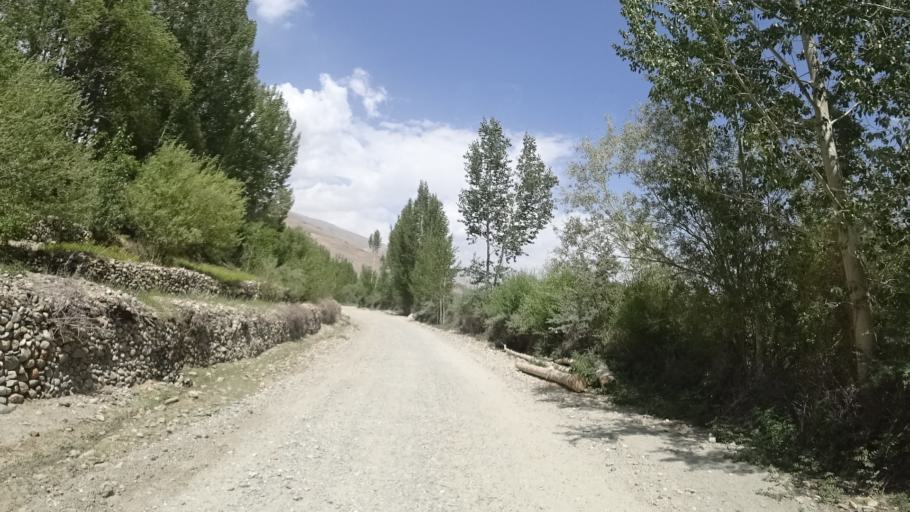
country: AF
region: Badakhshan
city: Khandud
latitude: 36.9420
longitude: 72.2261
